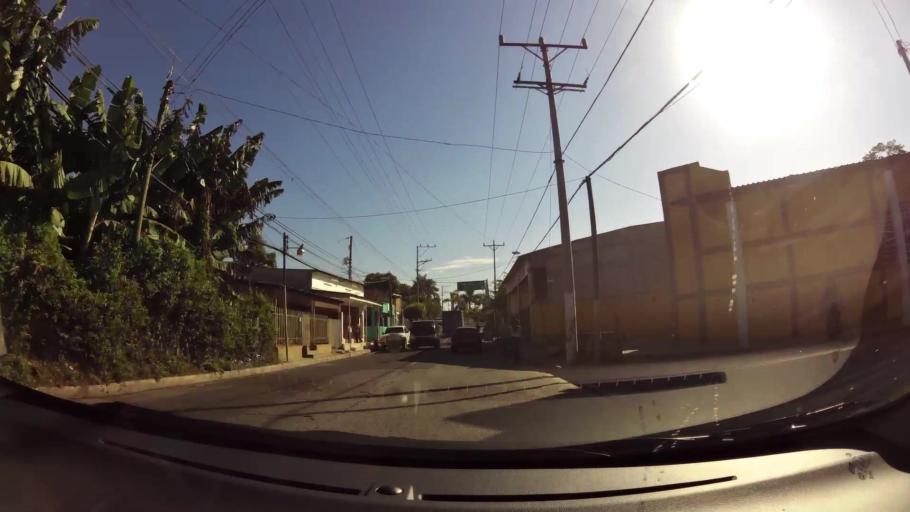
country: SV
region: Sonsonate
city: Sonzacate
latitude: 13.7377
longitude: -89.7106
